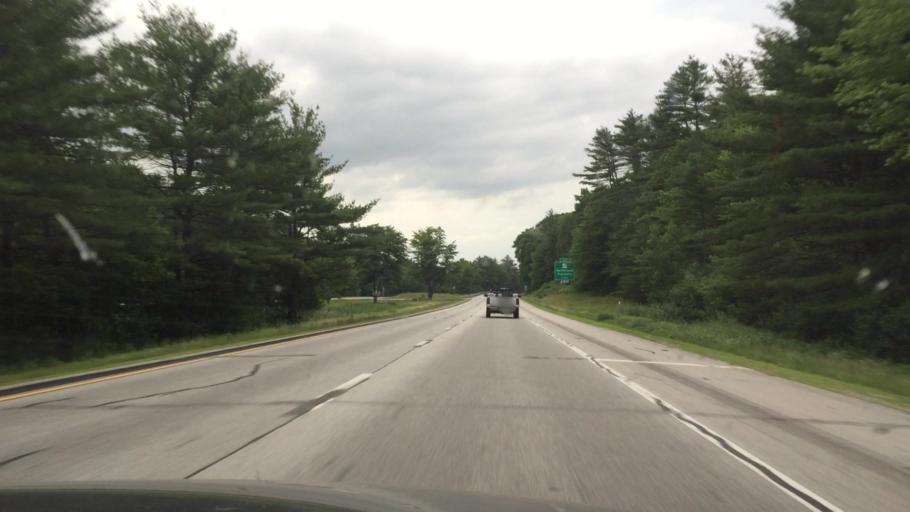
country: US
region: New Hampshire
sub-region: Merrimack County
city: Northfield
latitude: 43.4088
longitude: -71.5964
